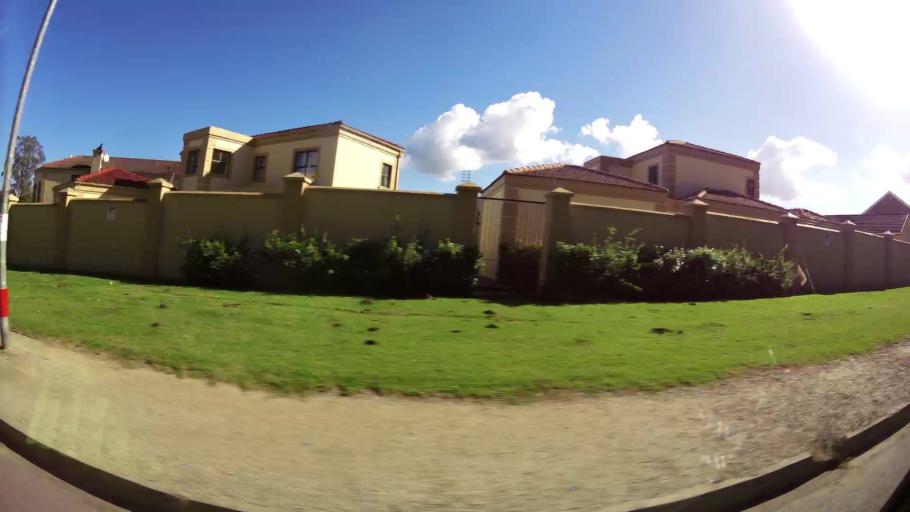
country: ZA
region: Western Cape
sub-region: Eden District Municipality
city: George
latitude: -33.9510
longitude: 22.4066
